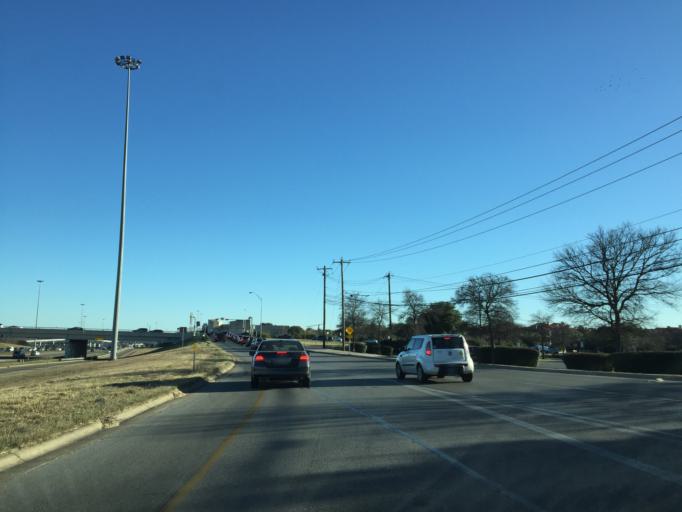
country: US
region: Texas
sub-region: Williamson County
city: Jollyville
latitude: 30.3909
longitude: -97.7465
